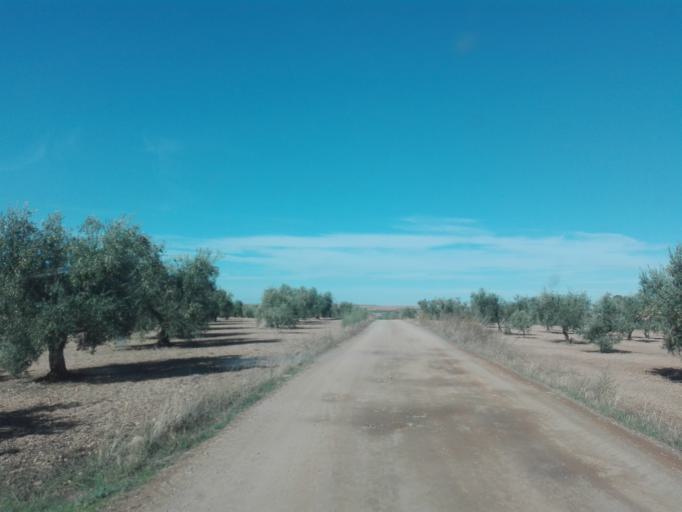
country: ES
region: Extremadura
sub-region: Provincia de Badajoz
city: Ahillones
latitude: 38.2817
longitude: -5.9023
